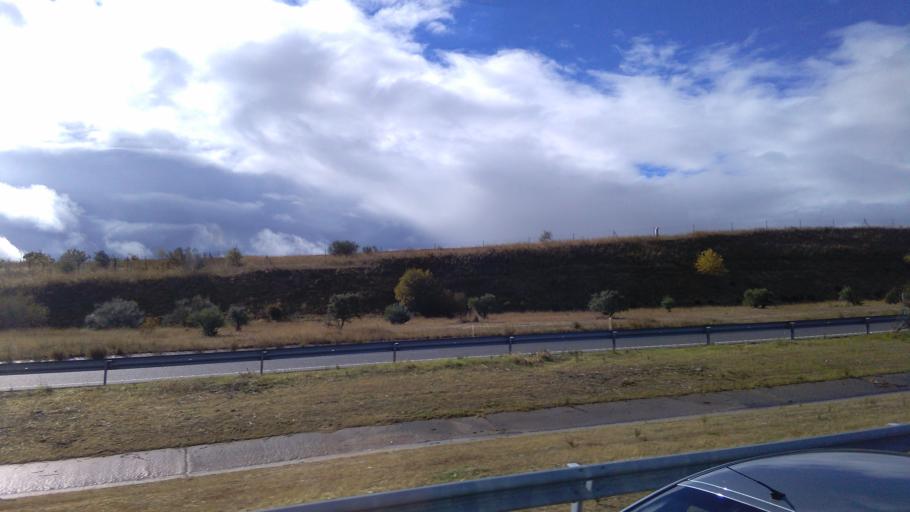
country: ES
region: Madrid
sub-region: Provincia de Madrid
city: Navalcarnero
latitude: 40.2657
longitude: -4.0246
